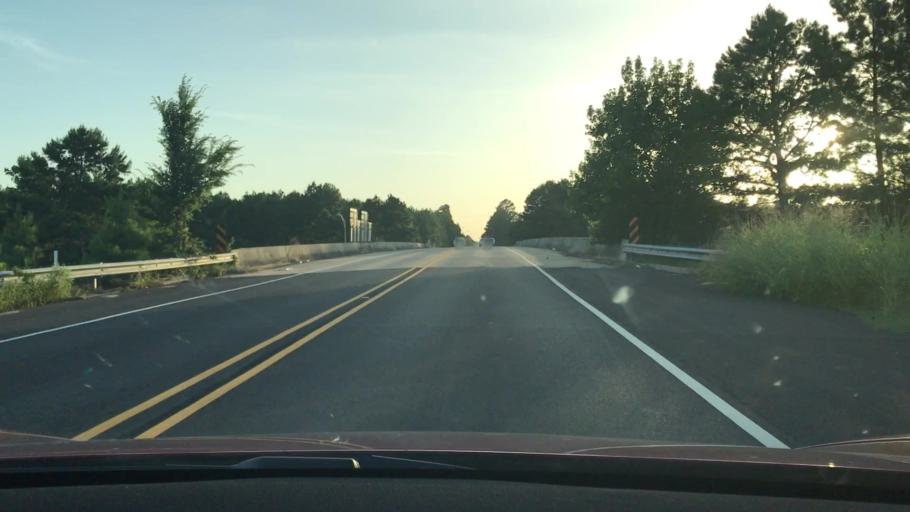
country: US
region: Louisiana
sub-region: Bossier Parish
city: Bossier City
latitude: 32.3910
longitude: -93.7511
